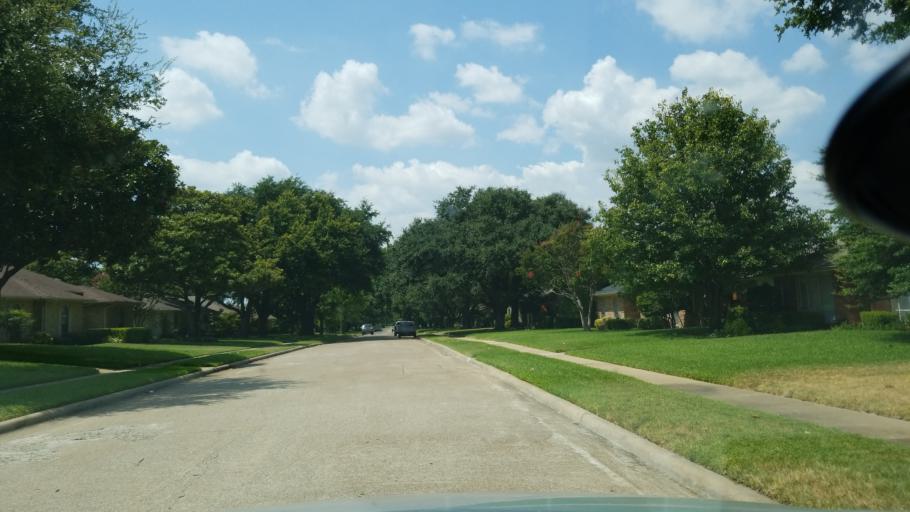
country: US
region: Texas
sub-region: Dallas County
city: Richardson
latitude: 32.9295
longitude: -96.7243
